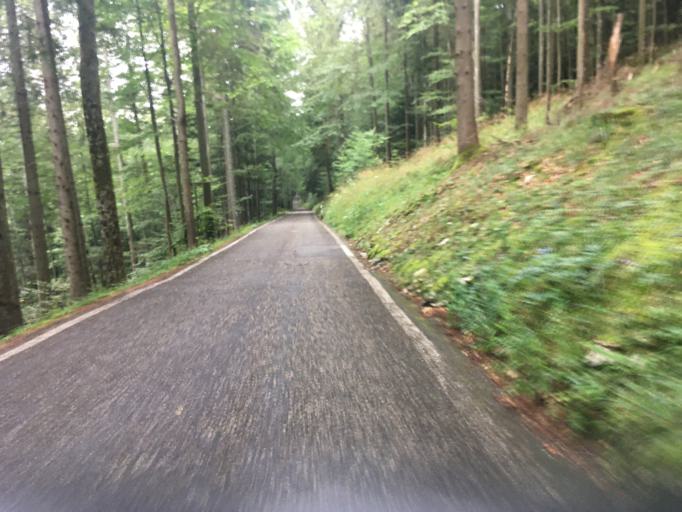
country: CH
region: Solothurn
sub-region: Bezirk Thal
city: Welschenrohr
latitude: 47.2576
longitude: 7.5031
